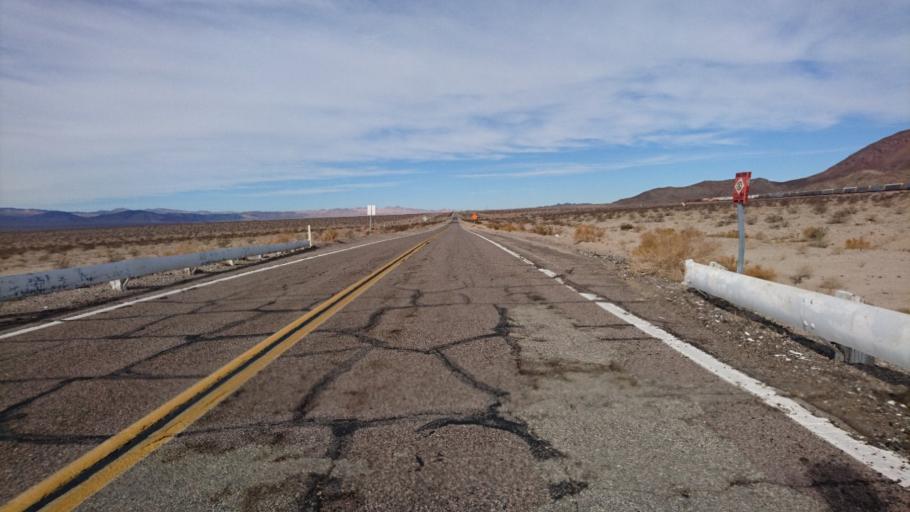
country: US
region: California
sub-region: San Bernardino County
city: Twentynine Palms
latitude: 34.5963
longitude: -115.9323
